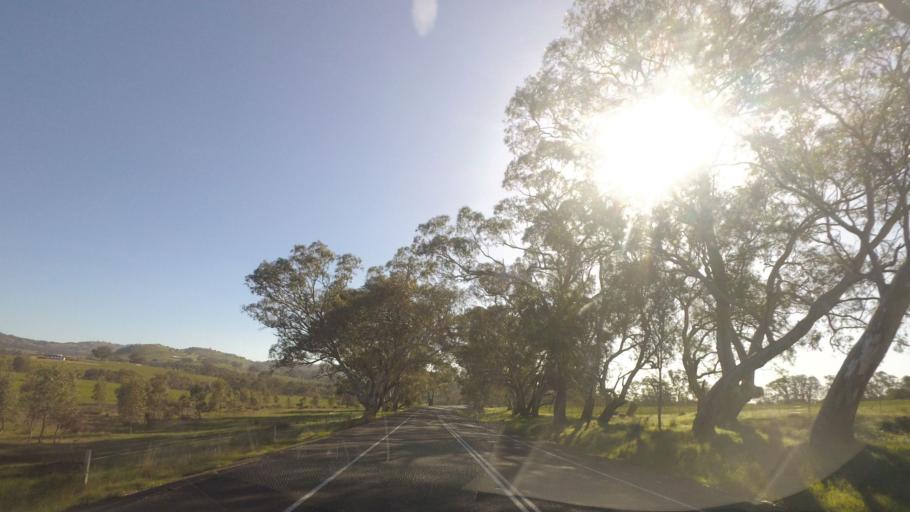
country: AU
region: Victoria
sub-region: Mount Alexander
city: Castlemaine
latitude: -36.9512
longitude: 144.3405
